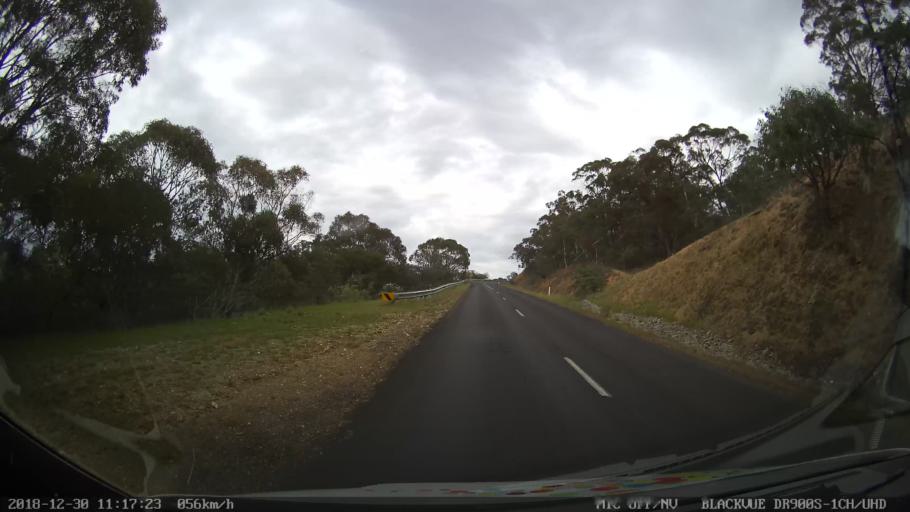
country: AU
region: New South Wales
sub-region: Snowy River
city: Jindabyne
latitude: -36.5366
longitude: 148.6989
